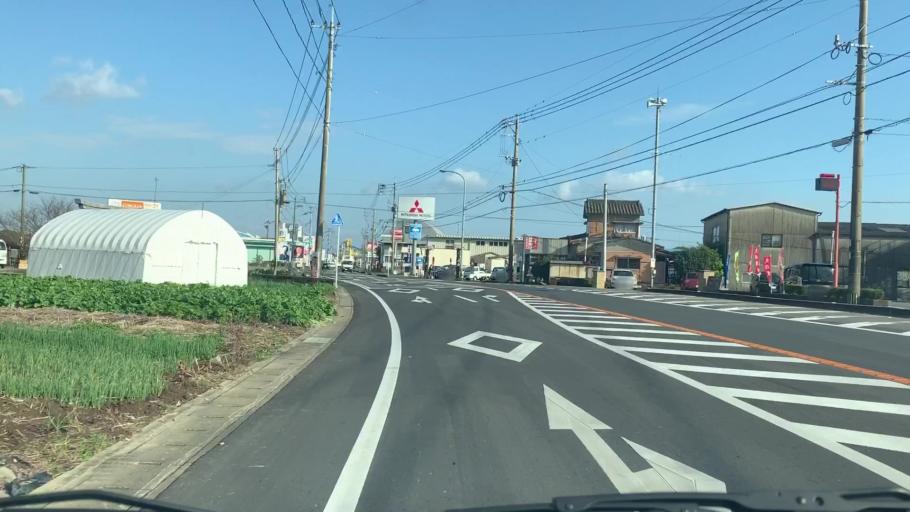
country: JP
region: Saga Prefecture
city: Kashima
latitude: 33.1221
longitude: 130.0841
